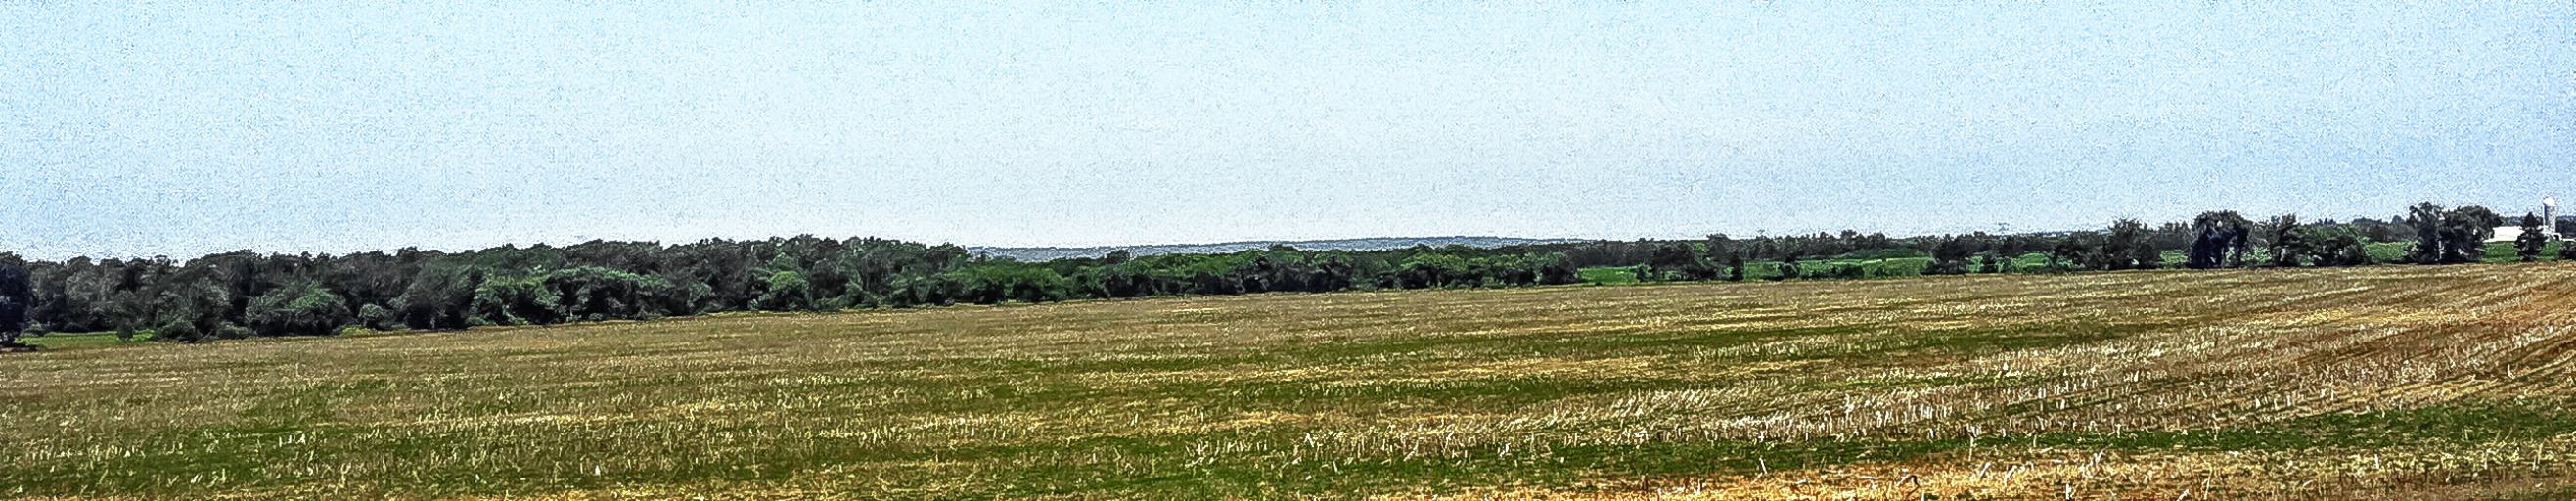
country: US
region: Wisconsin
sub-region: Chippewa County
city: Lake Wissota
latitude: 44.9960
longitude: -91.2872
